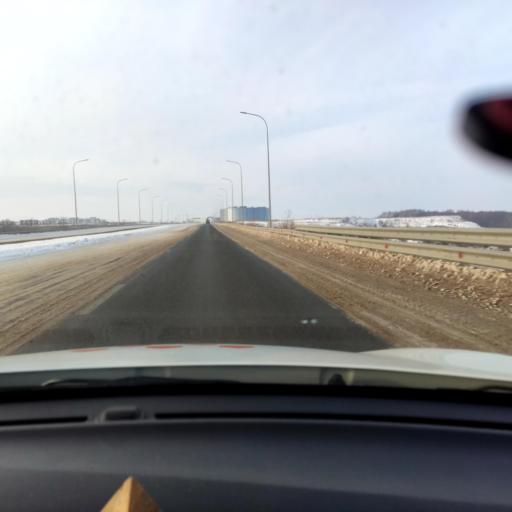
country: RU
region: Tatarstan
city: Sviyazhsk
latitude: 55.7464
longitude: 48.7670
